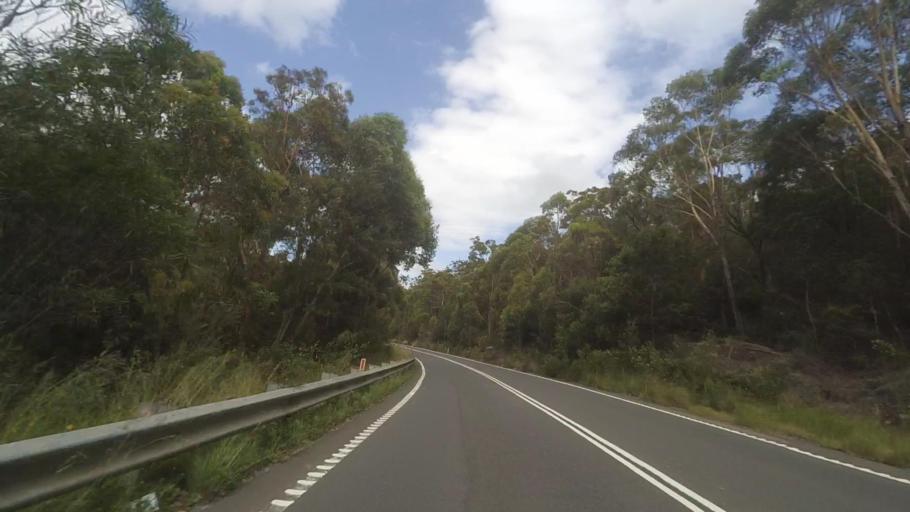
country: AU
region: New South Wales
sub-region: Sutherland Shire
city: Engadine
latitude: -34.0587
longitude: 150.9886
